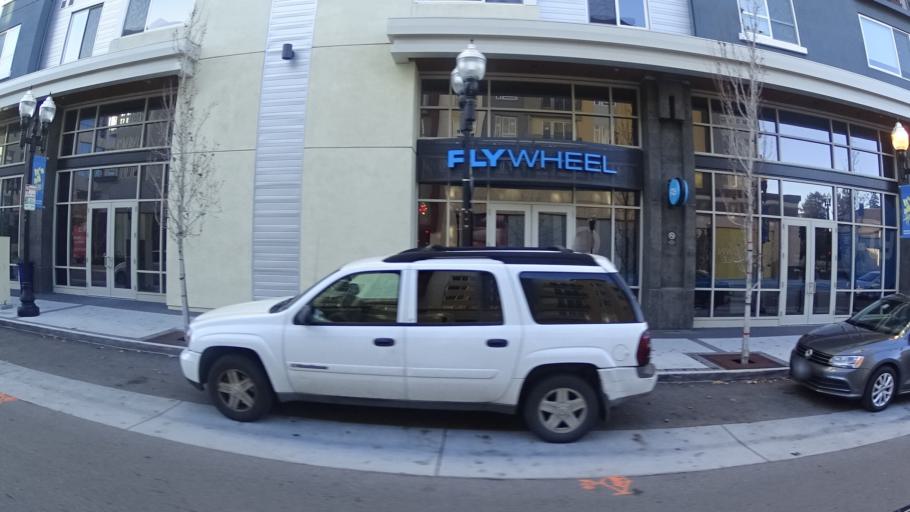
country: US
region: California
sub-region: Santa Clara County
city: Sunnyvale
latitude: 37.3766
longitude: -122.0330
